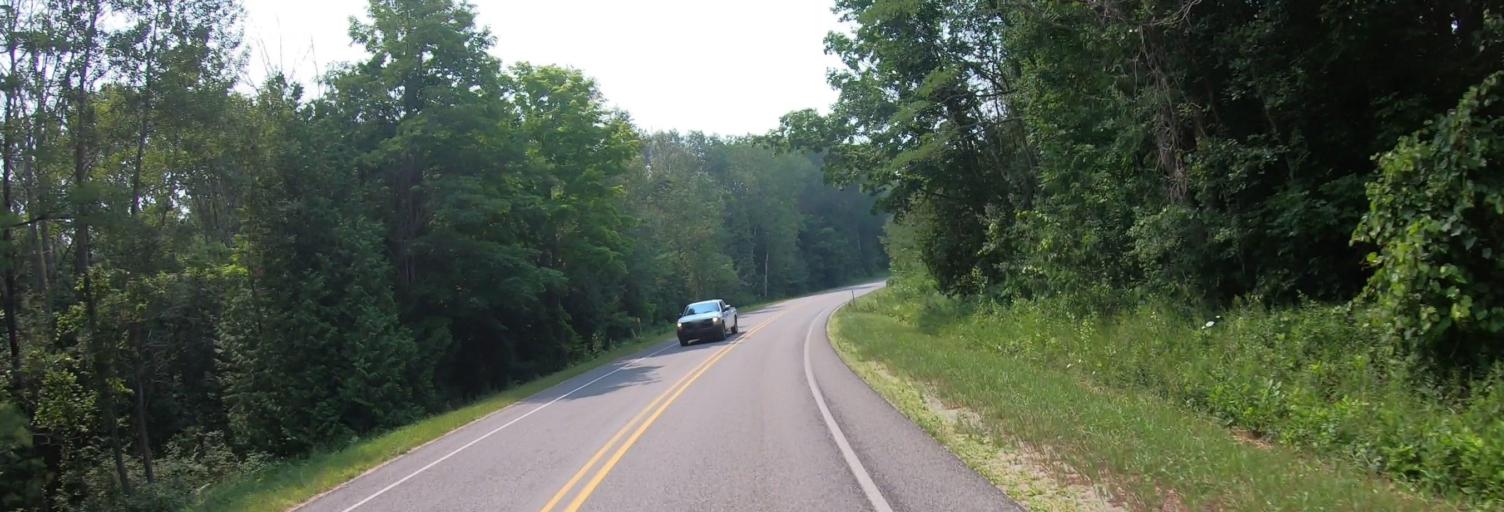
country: US
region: Michigan
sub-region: Leelanau County
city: Leland
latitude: 45.1633
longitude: -85.5637
